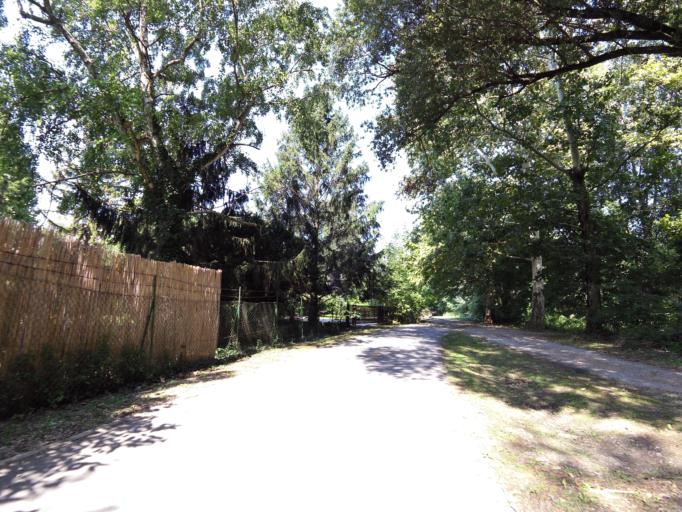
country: HU
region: Veszprem
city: Tihany
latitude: 46.8945
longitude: 17.8910
